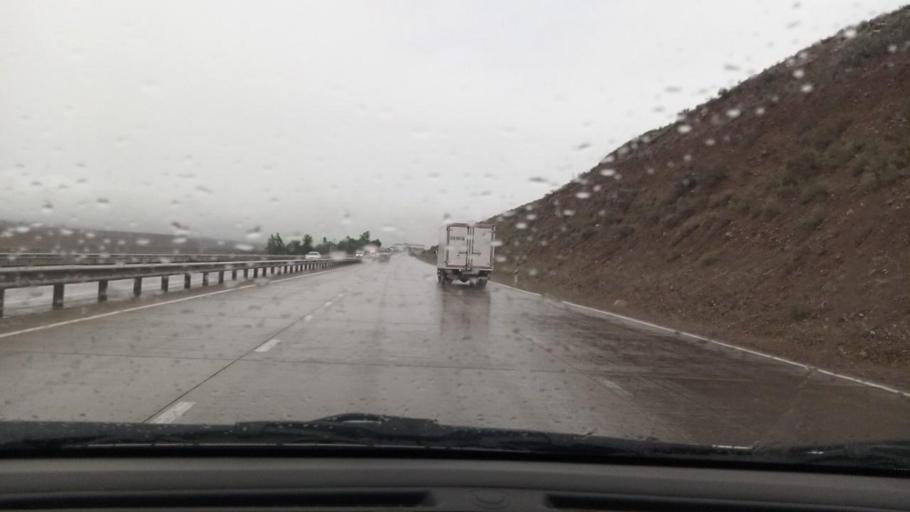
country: UZ
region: Namangan
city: Pop Shahri
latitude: 40.9248
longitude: 70.7263
